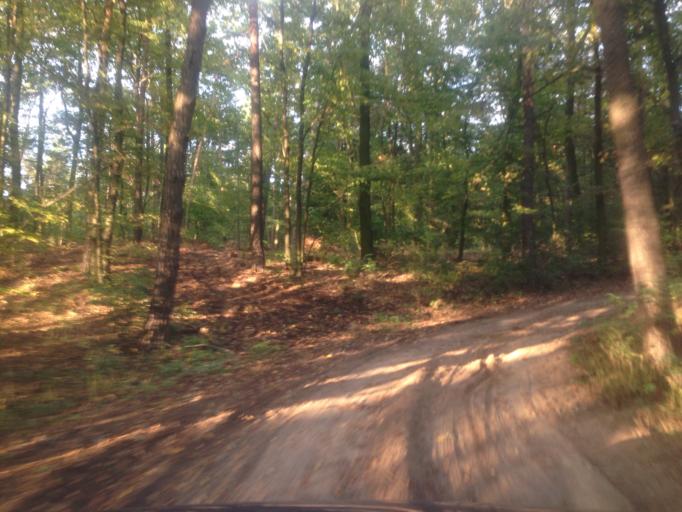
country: PL
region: Kujawsko-Pomorskie
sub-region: Powiat brodnicki
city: Gorzno
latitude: 53.2036
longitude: 19.6635
